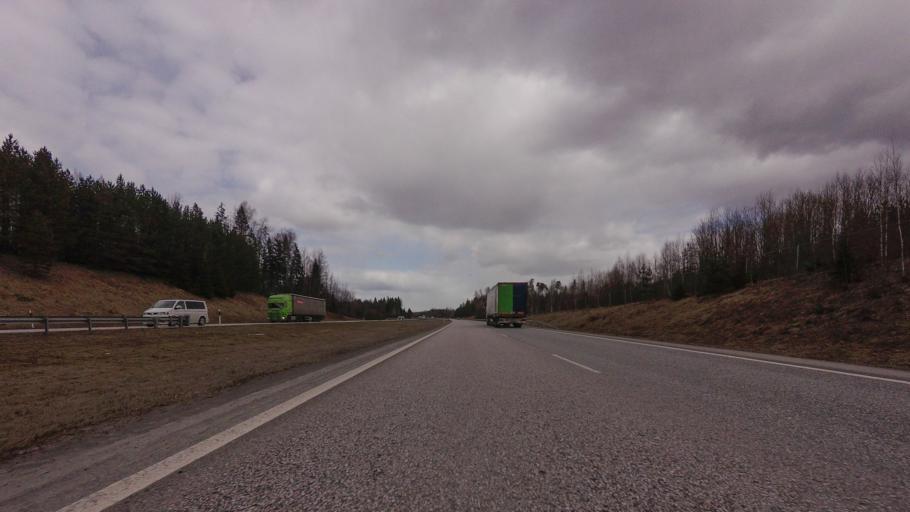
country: FI
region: Uusimaa
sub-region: Helsinki
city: Nurmijaervi
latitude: 60.3738
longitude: 24.8131
